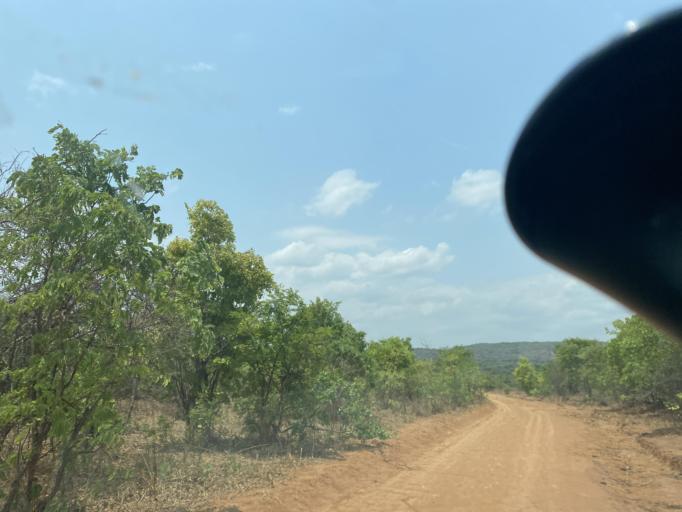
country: ZM
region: Lusaka
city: Chongwe
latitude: -15.5164
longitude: 28.8847
